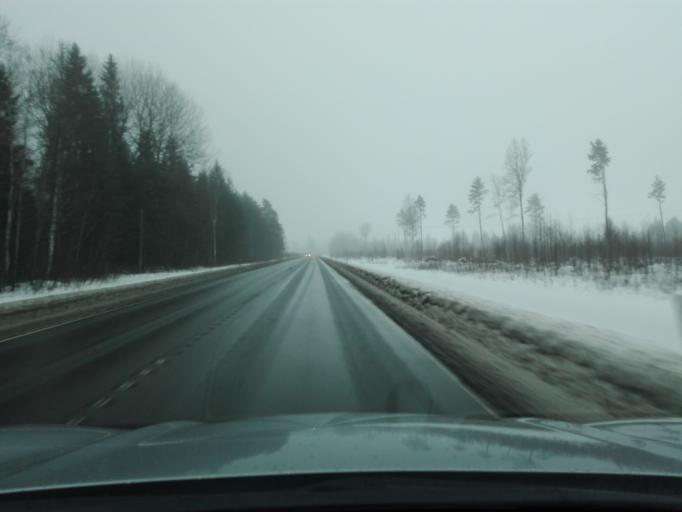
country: EE
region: Raplamaa
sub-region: Kohila vald
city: Kohila
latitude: 59.2369
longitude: 24.7641
